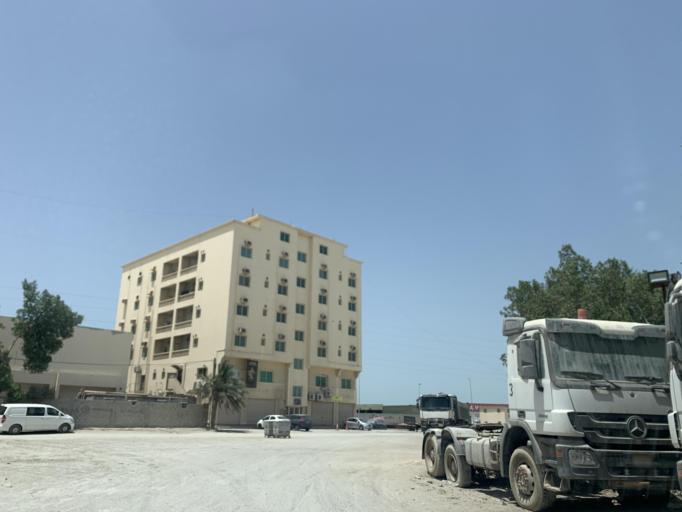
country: BH
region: Northern
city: Sitrah
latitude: 26.1754
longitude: 50.6060
